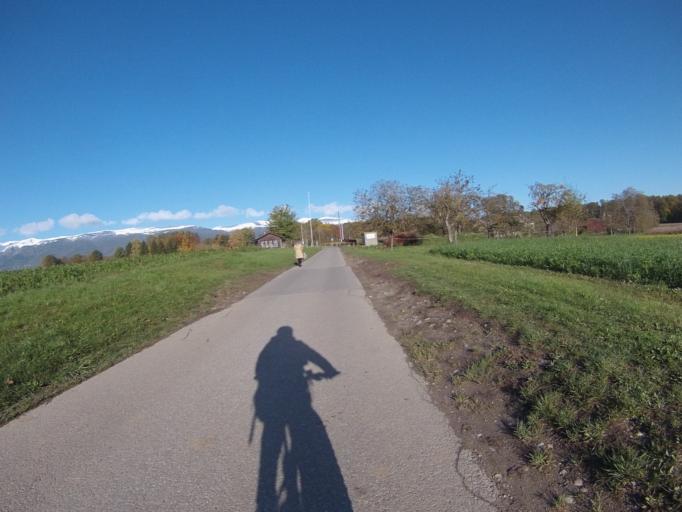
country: CH
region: Geneva
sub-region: Geneva
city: Meyrin
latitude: 46.2369
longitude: 6.0631
